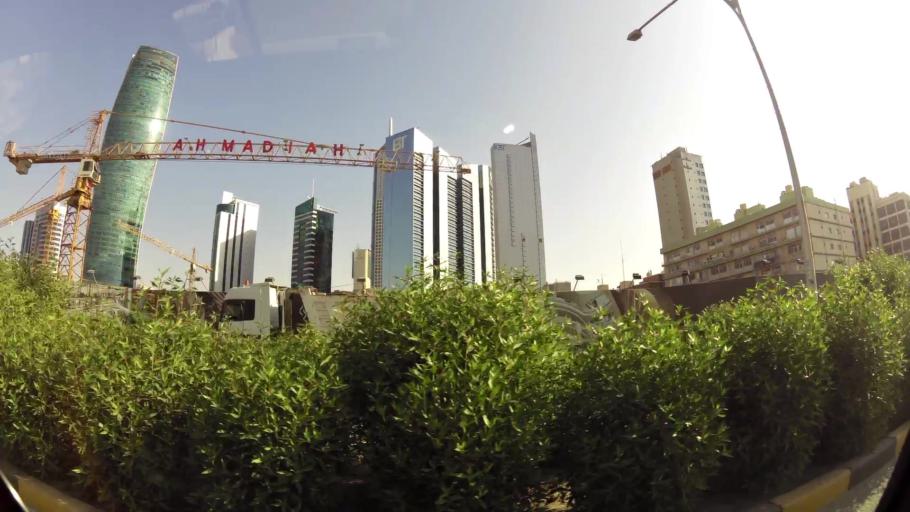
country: KW
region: Al Asimah
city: Kuwait City
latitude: 29.3726
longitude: 47.9868
